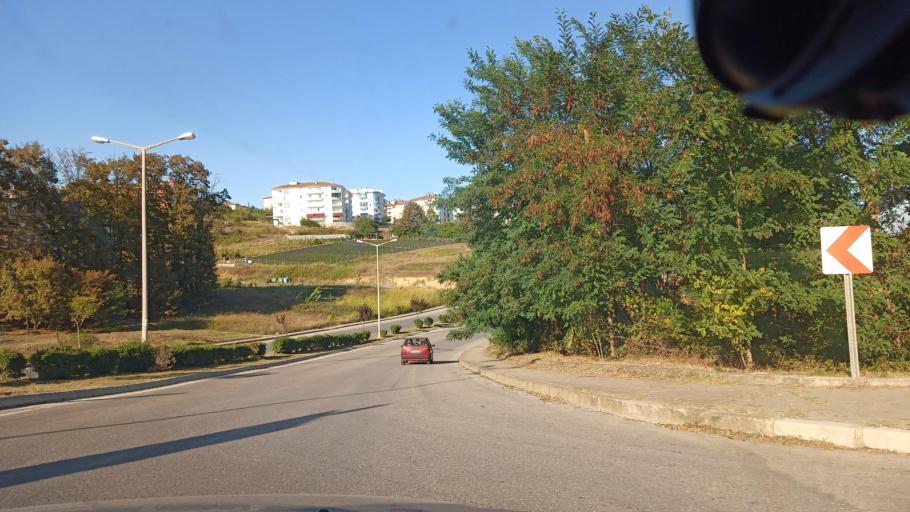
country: TR
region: Sakarya
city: Kazimpasa
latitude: 40.8535
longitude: 30.2890
